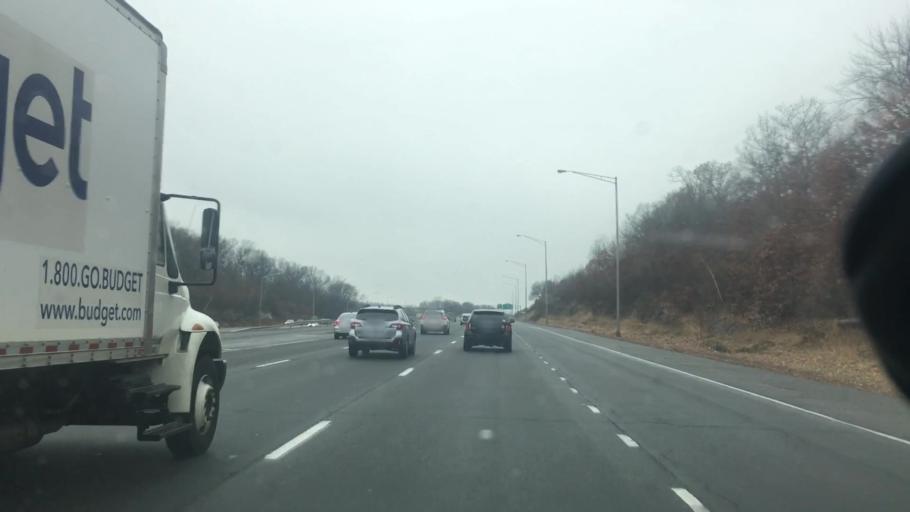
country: US
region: Connecticut
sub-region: Hartford County
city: Manchester
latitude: 41.8097
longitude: -72.5287
